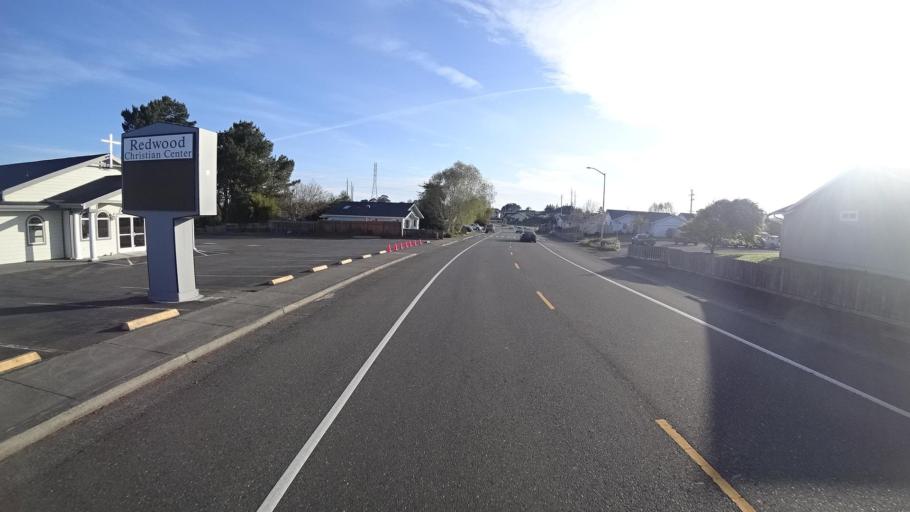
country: US
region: California
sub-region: Humboldt County
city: Humboldt Hill
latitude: 40.7366
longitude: -124.2018
